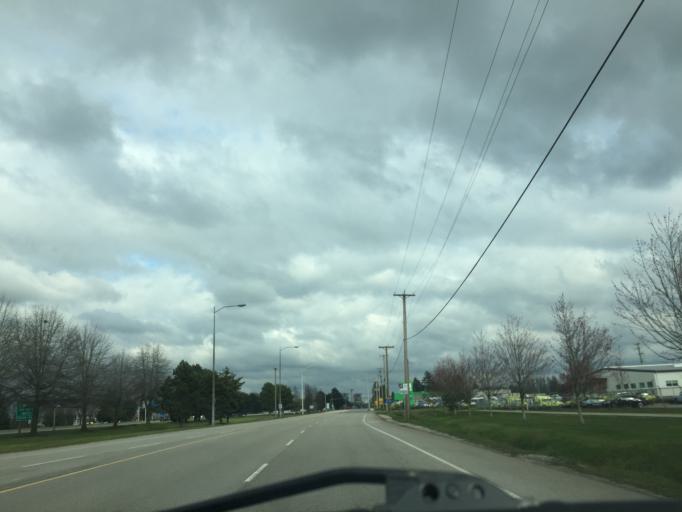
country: CA
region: British Columbia
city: Richmond
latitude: 49.1921
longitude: -123.1561
